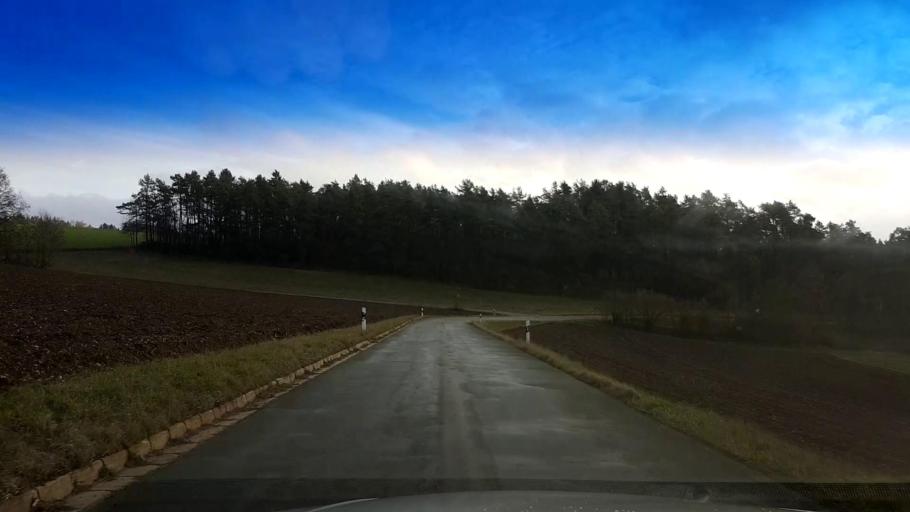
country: DE
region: Bavaria
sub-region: Upper Franconia
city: Poxdorf
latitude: 49.9306
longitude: 11.1265
